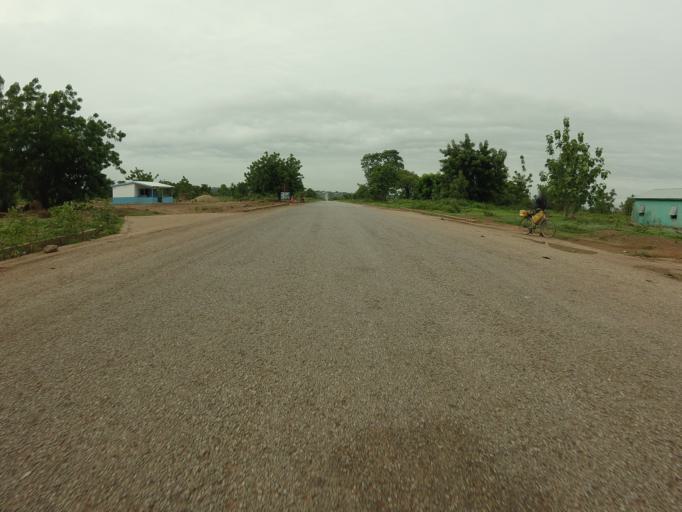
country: GH
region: Northern
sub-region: Yendi
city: Yendi
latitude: 9.5024
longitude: -0.0258
